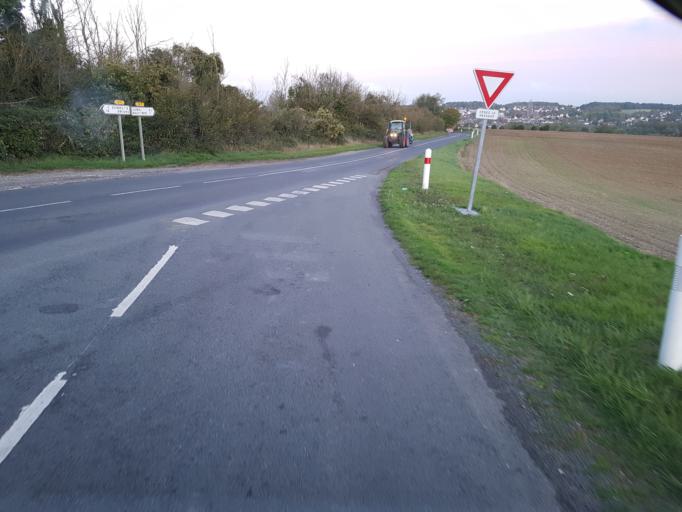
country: FR
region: Picardie
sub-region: Departement de la Somme
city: Ailly-sur-Noye
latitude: 49.7596
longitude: 2.3431
